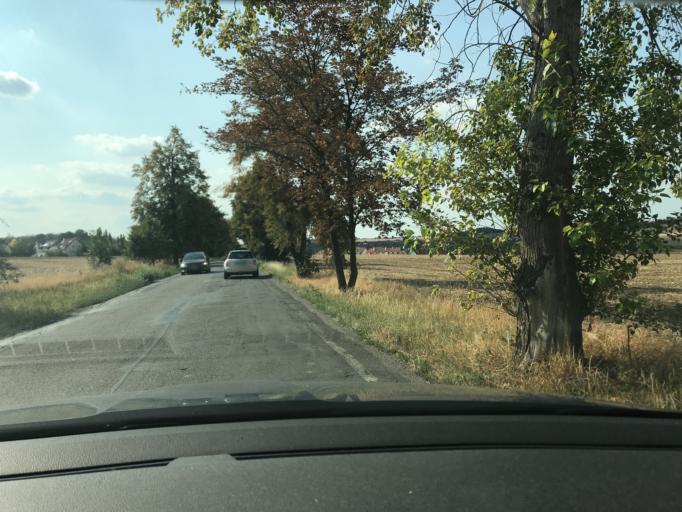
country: CZ
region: Central Bohemia
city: Velke Prilepy
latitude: 50.1558
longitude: 14.3258
